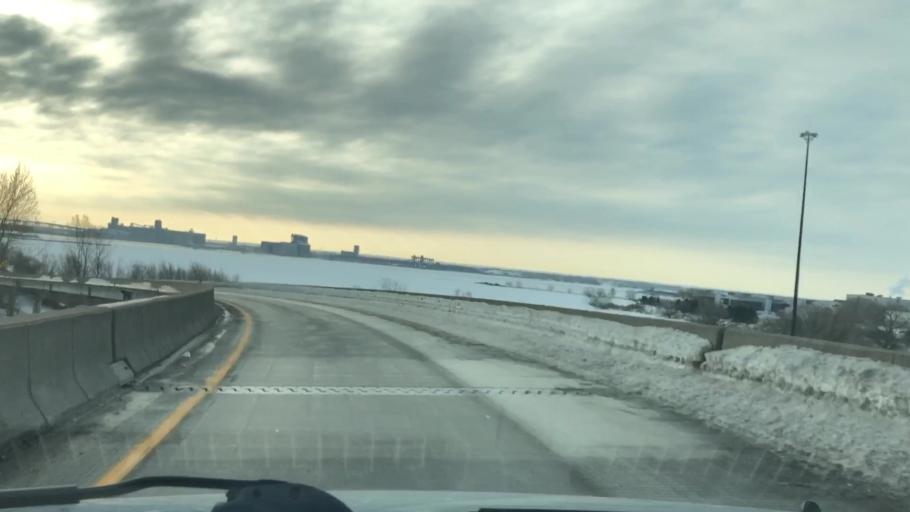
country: US
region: Minnesota
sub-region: Saint Louis County
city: Duluth
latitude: 46.7662
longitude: -92.1209
